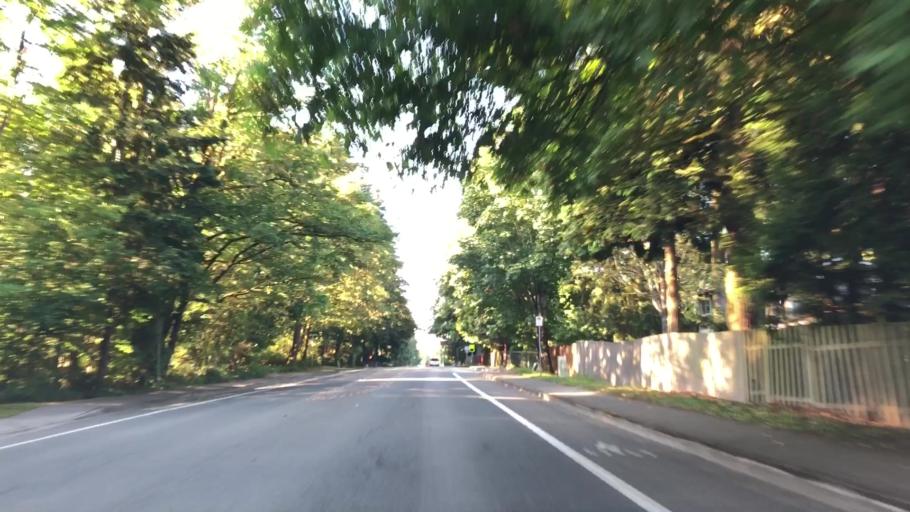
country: US
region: Washington
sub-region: King County
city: Redmond
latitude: 47.6947
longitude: -122.1187
